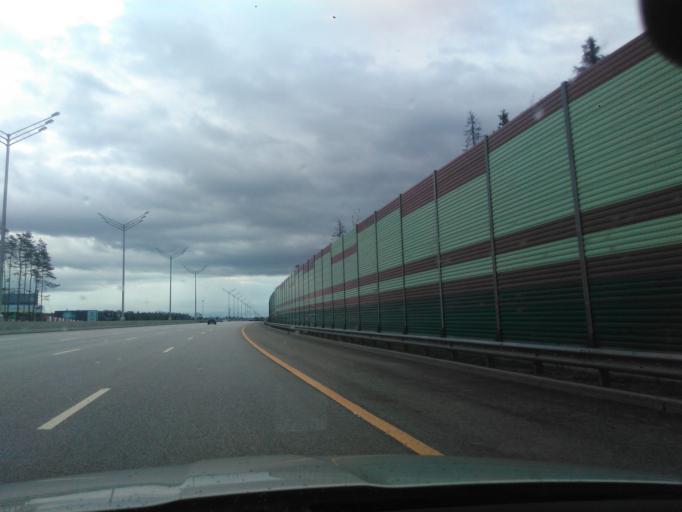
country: RU
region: Moskovskaya
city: Novopodrezkovo
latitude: 55.9593
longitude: 37.4023
